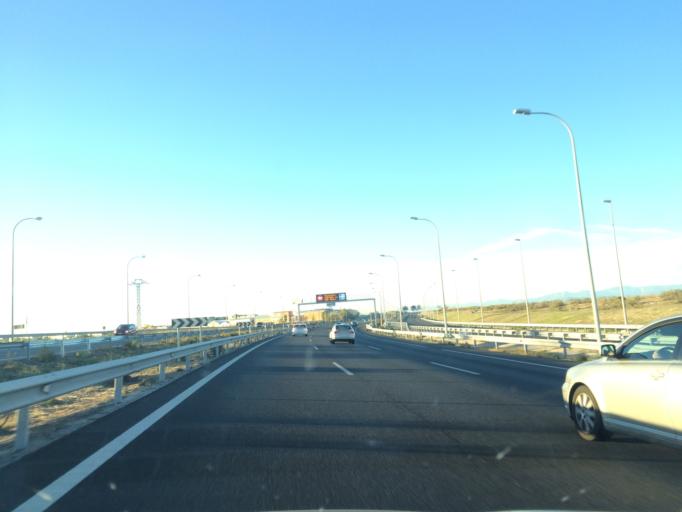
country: ES
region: Madrid
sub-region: Provincia de Madrid
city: Alcorcon
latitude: 40.3859
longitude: -3.8259
